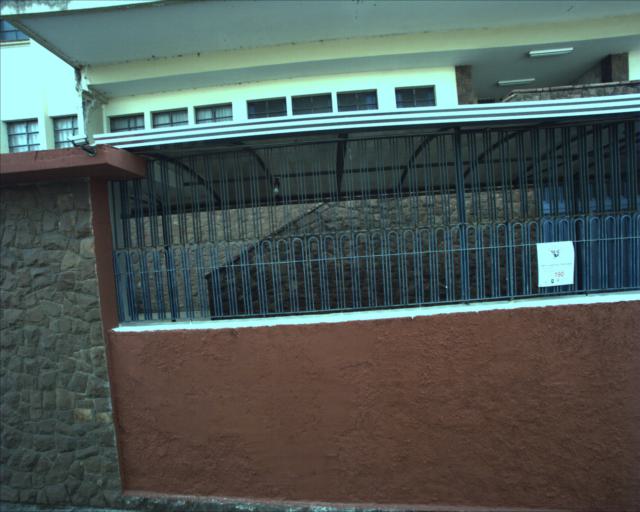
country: BR
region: Sao Paulo
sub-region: Sorocaba
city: Sorocaba
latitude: -23.4984
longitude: -47.4534
